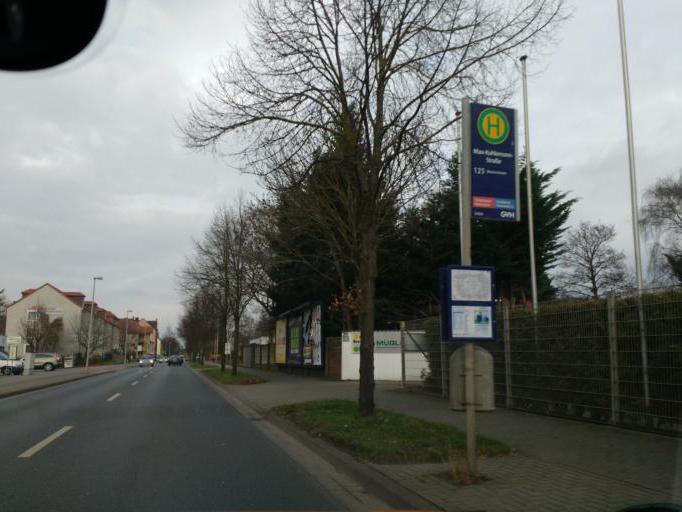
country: DE
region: Lower Saxony
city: Laatzen
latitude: 52.3710
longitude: 9.8623
